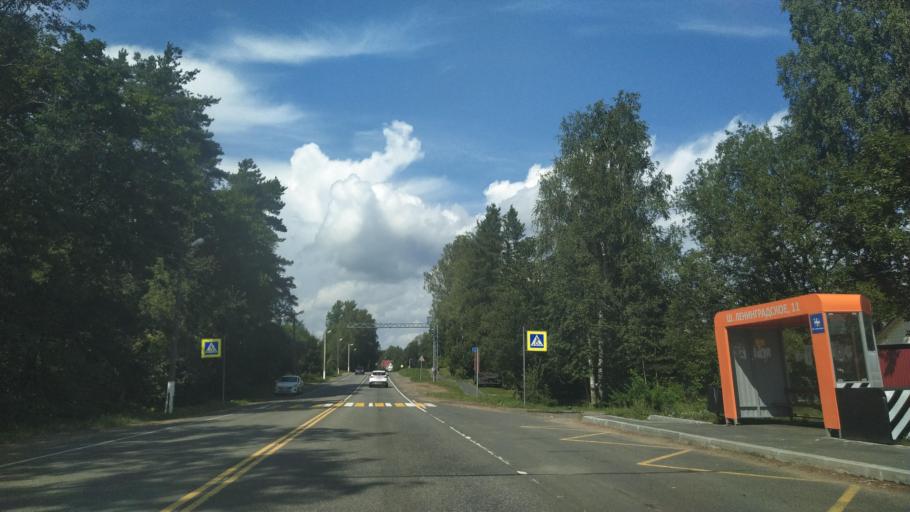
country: RU
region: Leningrad
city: Toksovo
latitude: 60.1447
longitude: 30.5265
